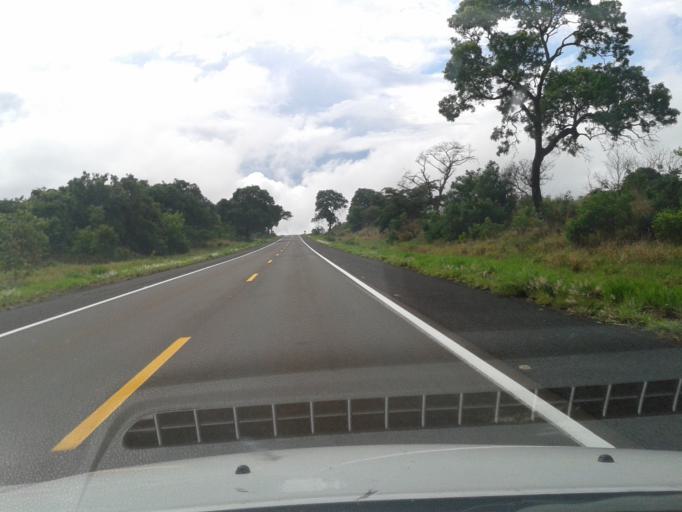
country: BR
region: Minas Gerais
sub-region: Campina Verde
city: Campina Verde
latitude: -19.4377
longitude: -49.5733
